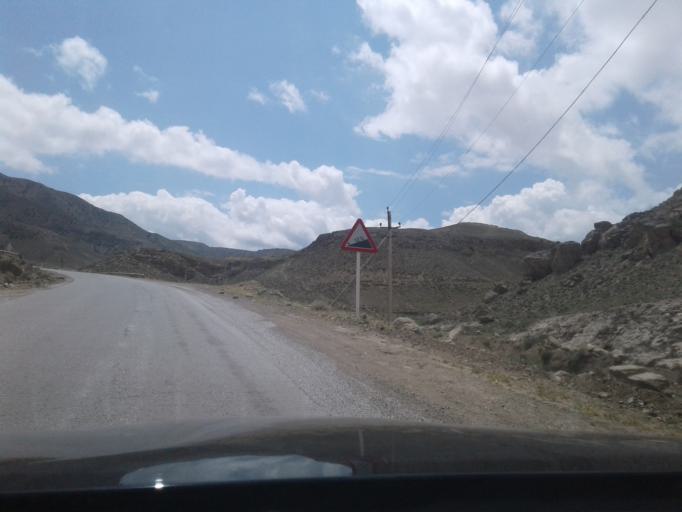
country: TM
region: Ahal
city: Baharly
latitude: 38.4606
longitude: 57.0367
